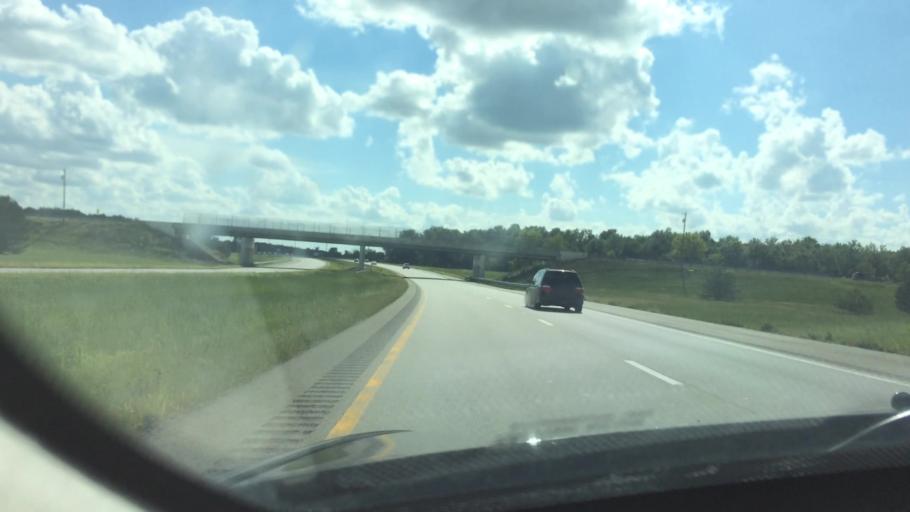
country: US
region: Ohio
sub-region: Shelby County
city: Sidney
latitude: 40.3150
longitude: -84.1741
